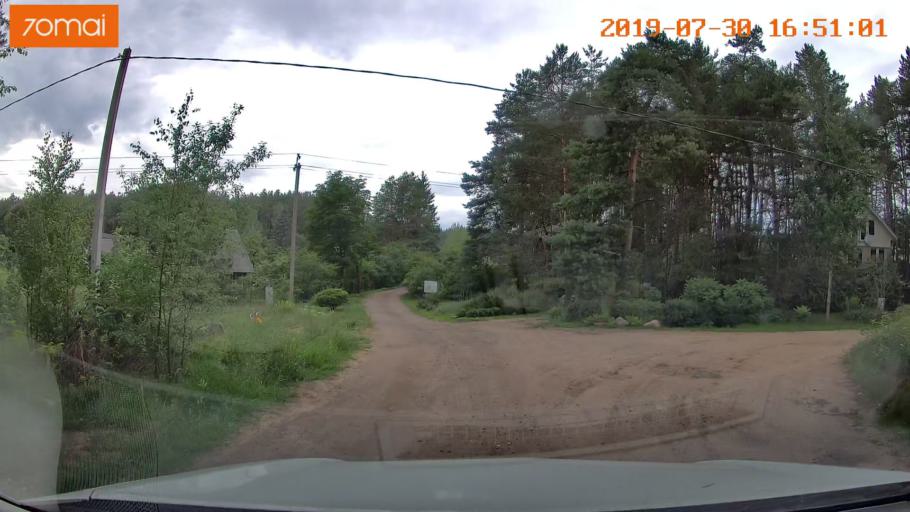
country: LT
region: Vilnius County
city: Rasos
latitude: 54.7436
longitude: 25.3915
